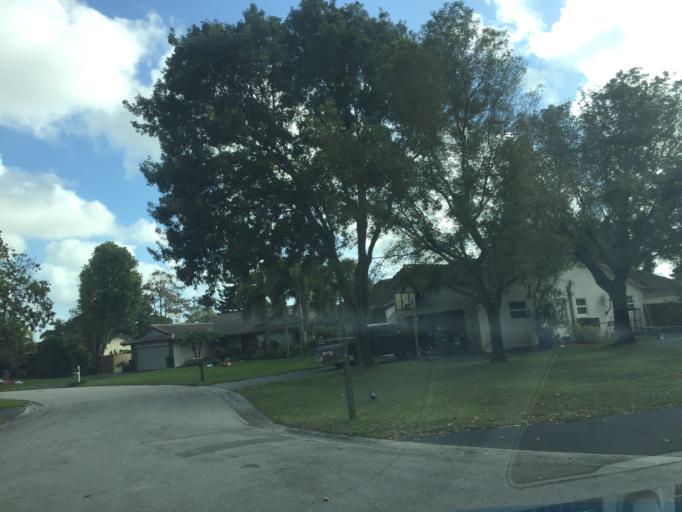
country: US
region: Florida
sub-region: Broward County
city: Tamarac
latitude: 26.2316
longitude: -80.2435
